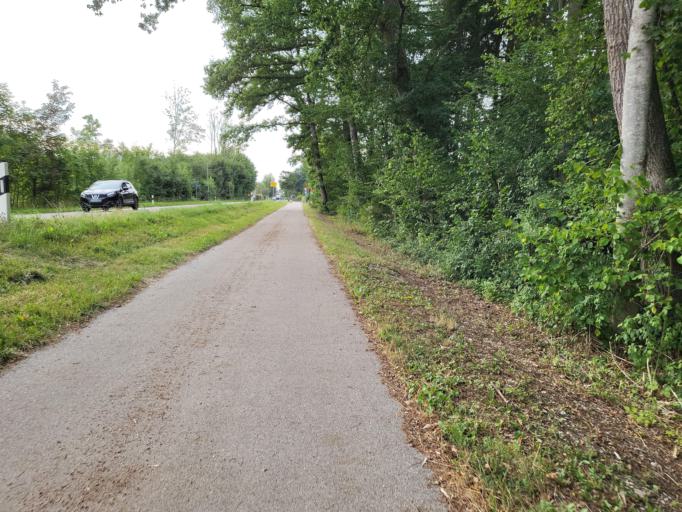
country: DE
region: Bavaria
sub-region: Upper Bavaria
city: Hohenkirchen-Siegertsbrunn
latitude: 48.0116
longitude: 11.7191
